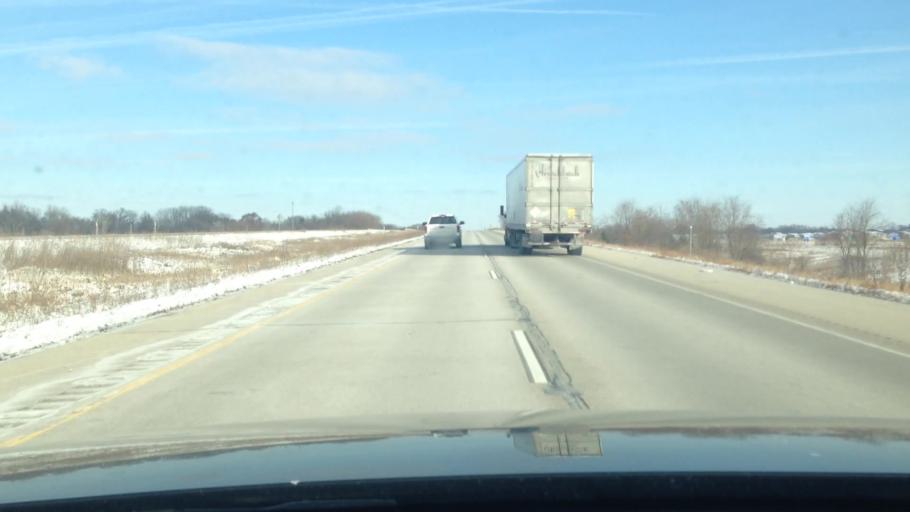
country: US
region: Wisconsin
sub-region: Walworth County
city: East Troy
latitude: 42.7887
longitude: -88.3865
